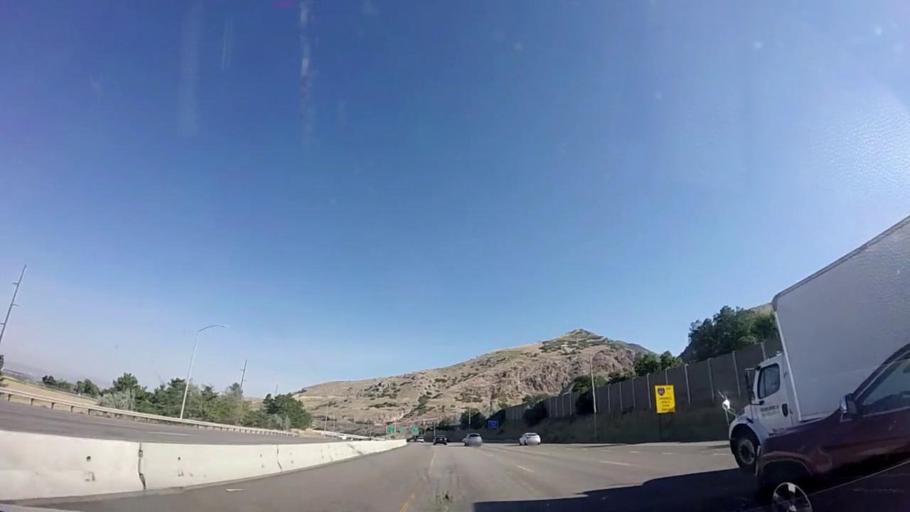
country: US
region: Utah
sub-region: Salt Lake County
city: East Millcreek
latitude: 40.7033
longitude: -111.7952
